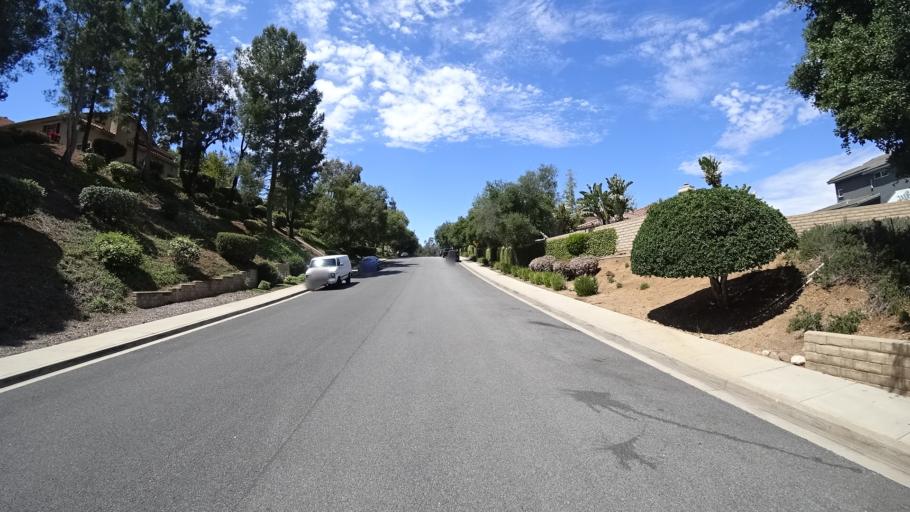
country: US
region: California
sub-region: Ventura County
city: Casa Conejo
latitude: 34.1811
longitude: -118.9037
